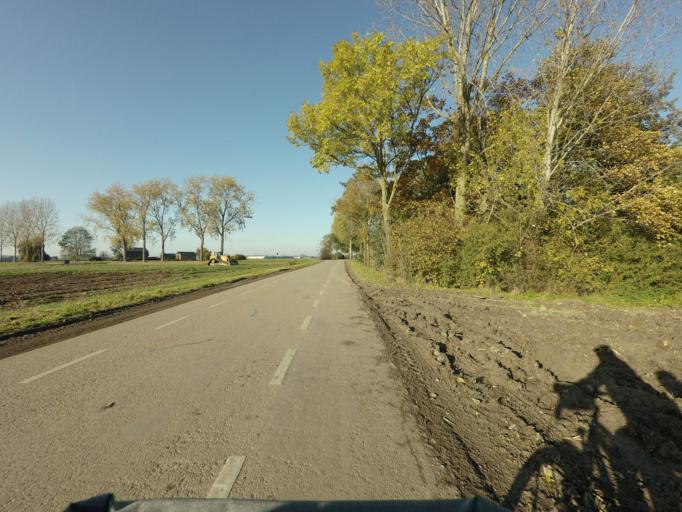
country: NL
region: North Brabant
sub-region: Gemeente Woudrichem
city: Woudrichem
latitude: 51.7672
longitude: 5.0490
